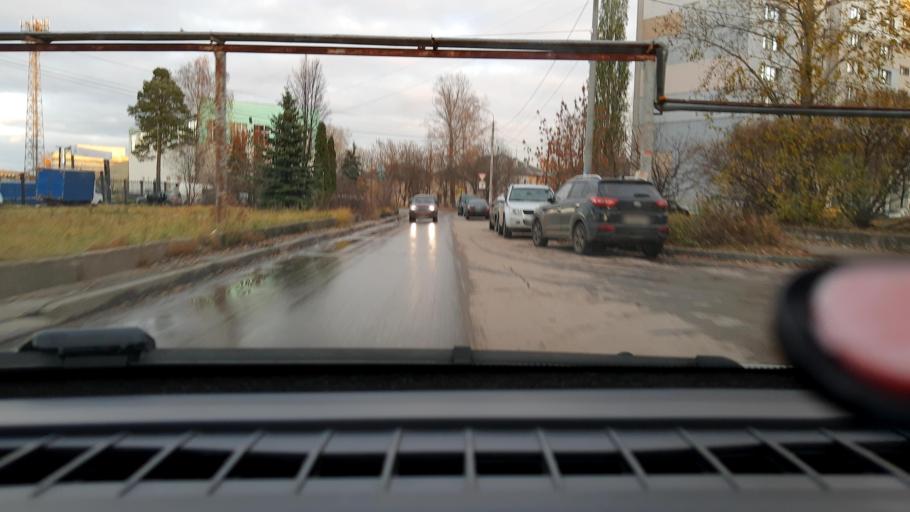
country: RU
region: Nizjnij Novgorod
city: Gorbatovka
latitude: 56.2922
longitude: 43.8444
